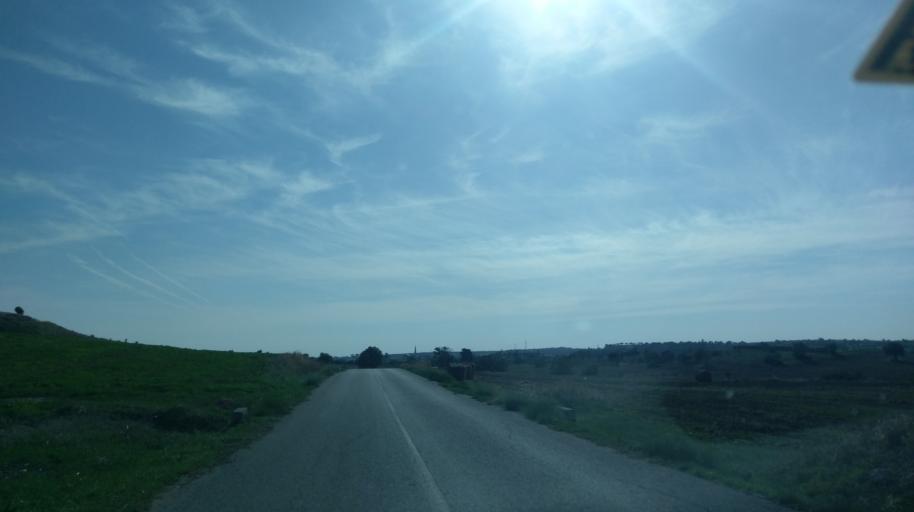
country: CY
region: Ammochostos
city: Trikomo
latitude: 35.3378
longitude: 33.9296
